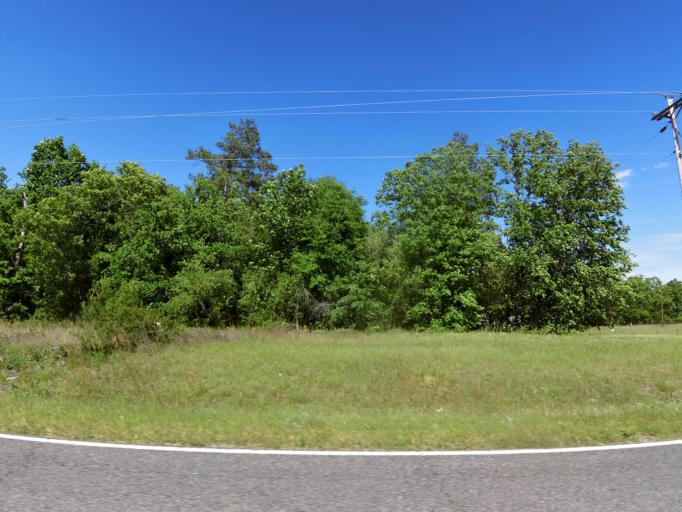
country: US
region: South Carolina
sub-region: Barnwell County
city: Williston
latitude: 33.4634
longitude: -81.5008
